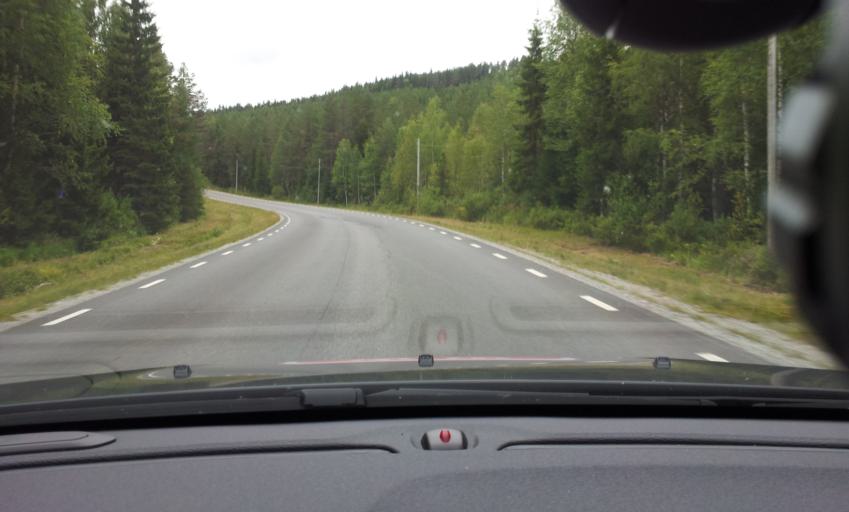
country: SE
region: Jaemtland
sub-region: Braecke Kommun
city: Braecke
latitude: 63.0572
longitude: 15.3273
